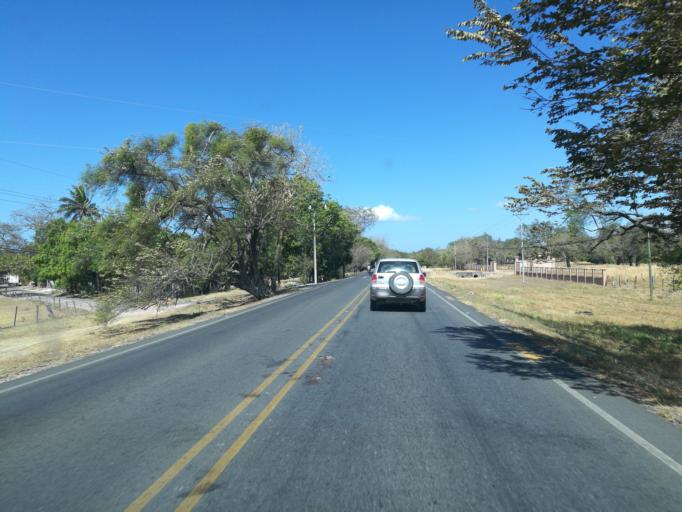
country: CR
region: Guanacaste
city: Liberia
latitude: 10.6469
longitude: -85.4590
